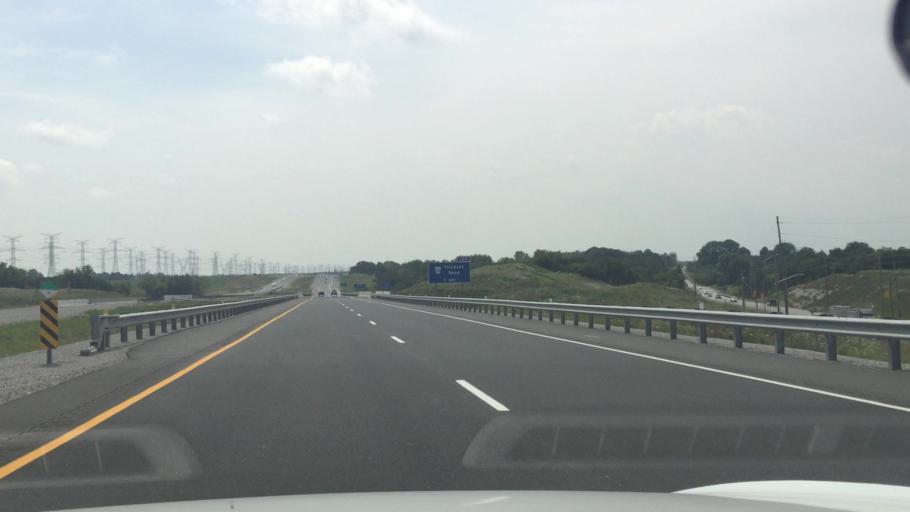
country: CA
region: Ontario
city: Oshawa
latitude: 43.9628
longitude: -78.9219
